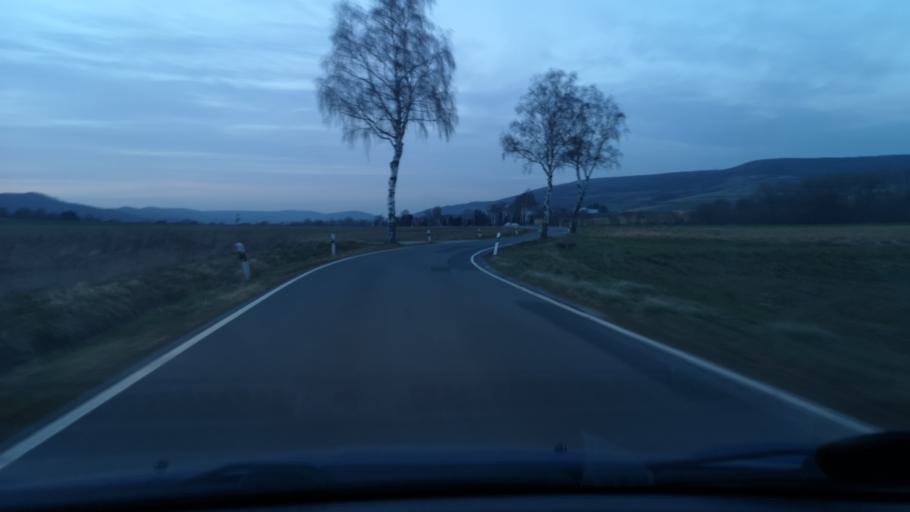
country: DE
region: Lower Saxony
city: Weenzen
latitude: 52.0068
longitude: 9.6349
